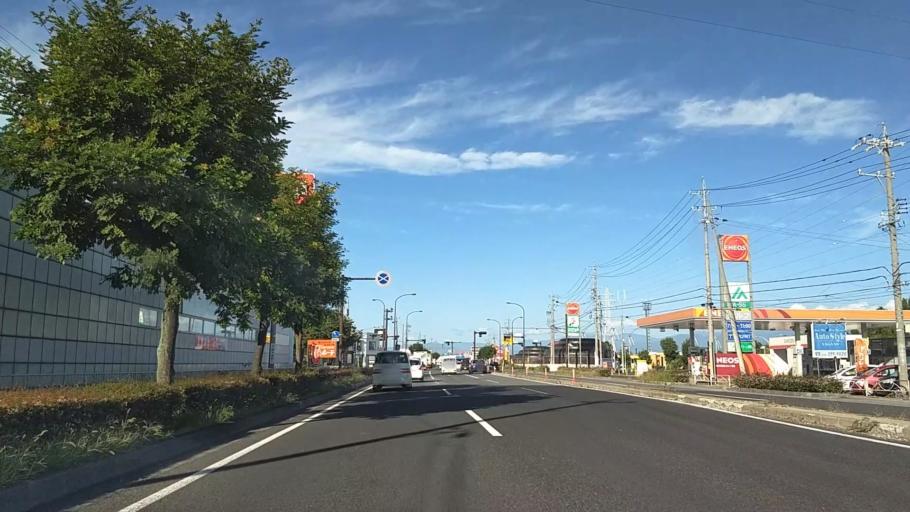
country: JP
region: Nagano
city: Nagano-shi
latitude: 36.5809
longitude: 138.1615
